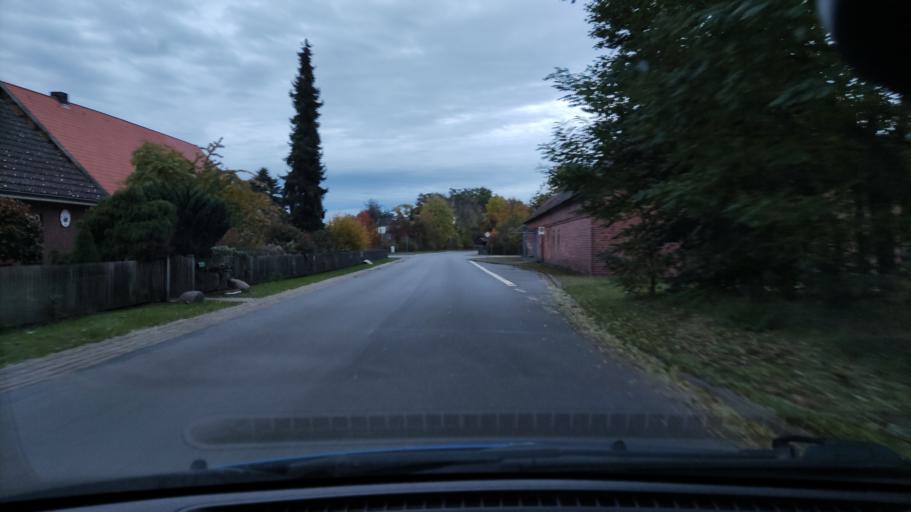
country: DE
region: Lower Saxony
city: Prezelle
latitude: 52.9435
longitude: 11.3932
